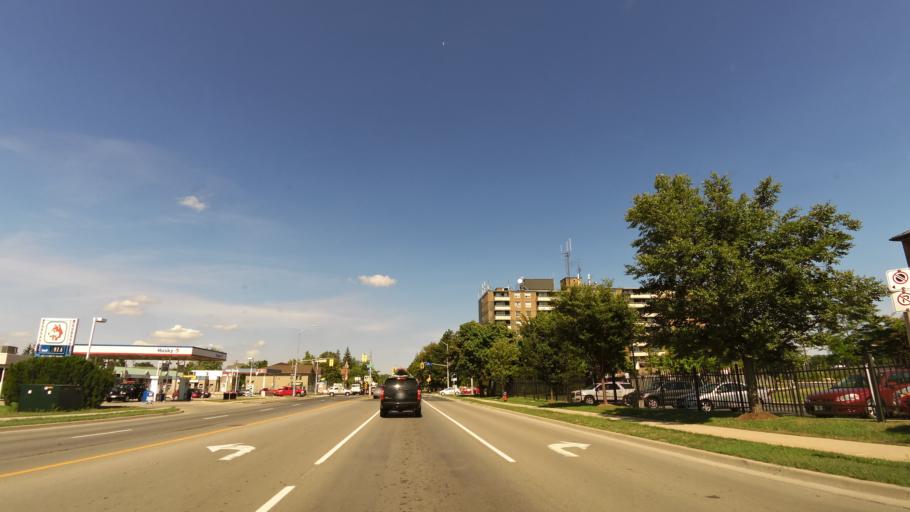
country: CA
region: Ontario
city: Burlington
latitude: 43.3304
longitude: -79.8963
